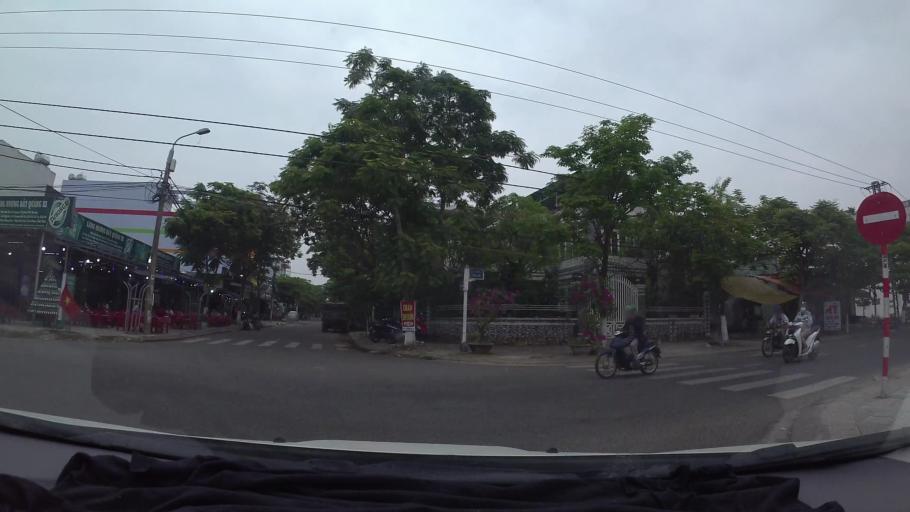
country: VN
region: Da Nang
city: Thanh Khe
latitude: 16.0543
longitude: 108.1771
